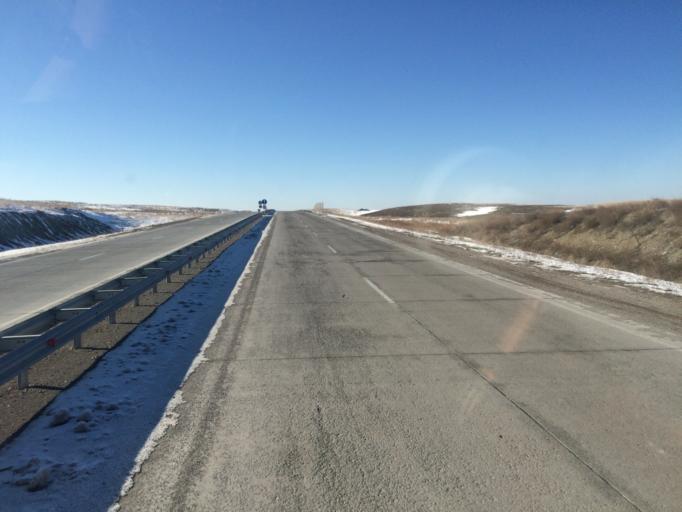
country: KZ
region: Zhambyl
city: Georgiyevka
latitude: 43.3633
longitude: 74.6913
